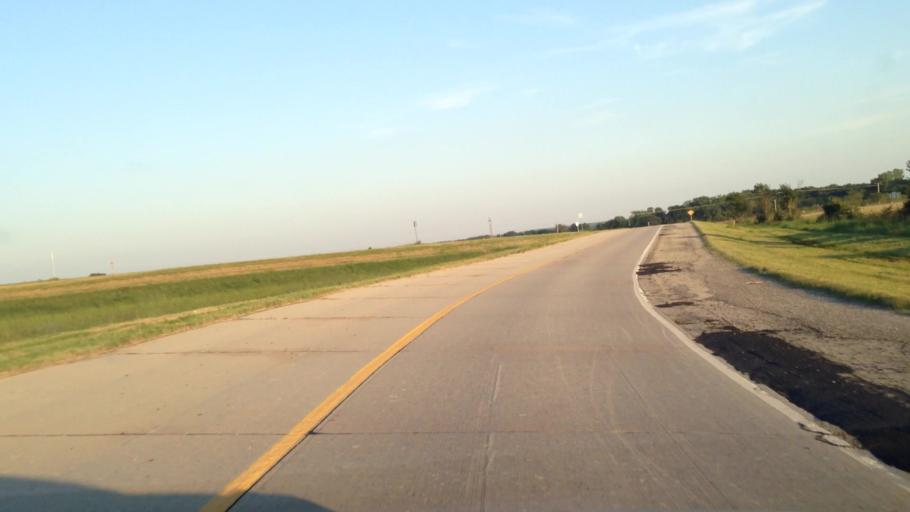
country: US
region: Oklahoma
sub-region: Ottawa County
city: Afton
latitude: 36.7182
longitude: -94.9301
